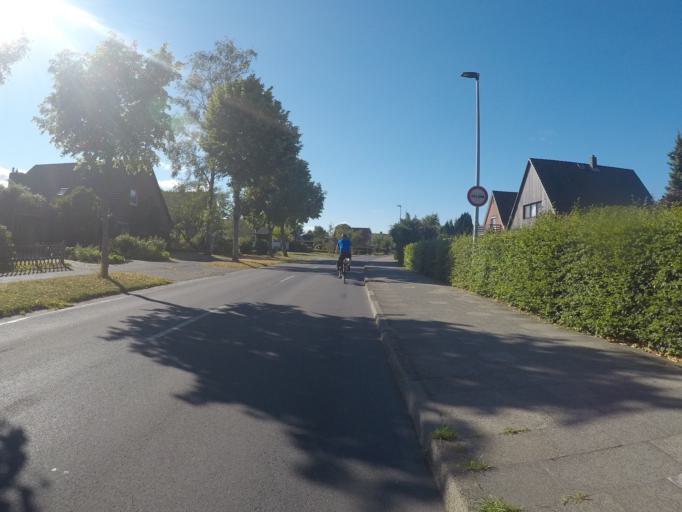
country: DE
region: Lower Saxony
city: Otterndorf
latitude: 53.8161
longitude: 8.8992
